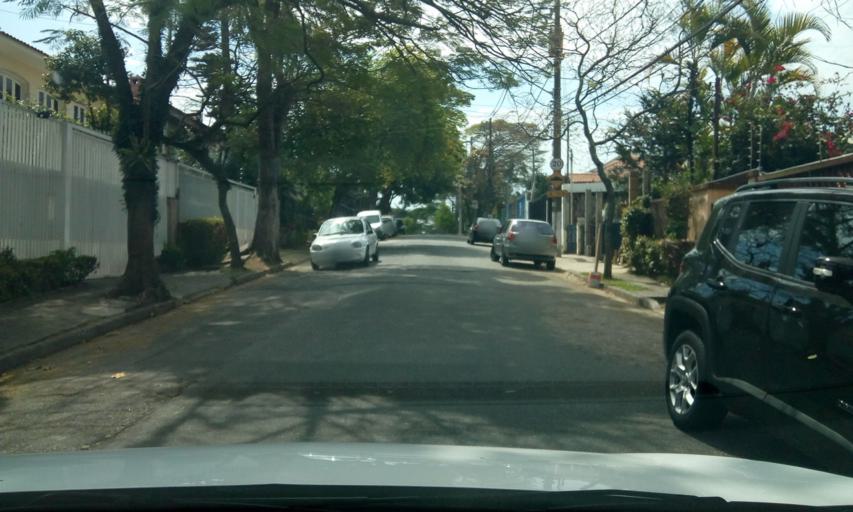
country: BR
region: Sao Paulo
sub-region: Taboao Da Serra
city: Taboao da Serra
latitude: -23.5937
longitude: -46.7261
